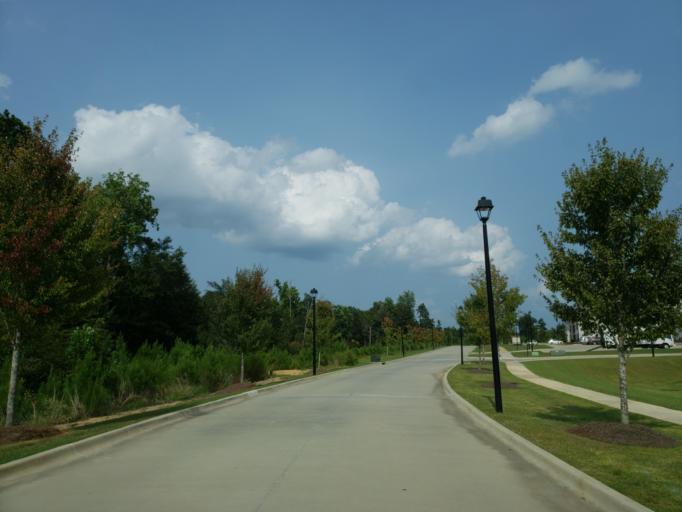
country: US
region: Mississippi
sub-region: Forrest County
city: Hattiesburg
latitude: 31.2765
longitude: -89.3243
